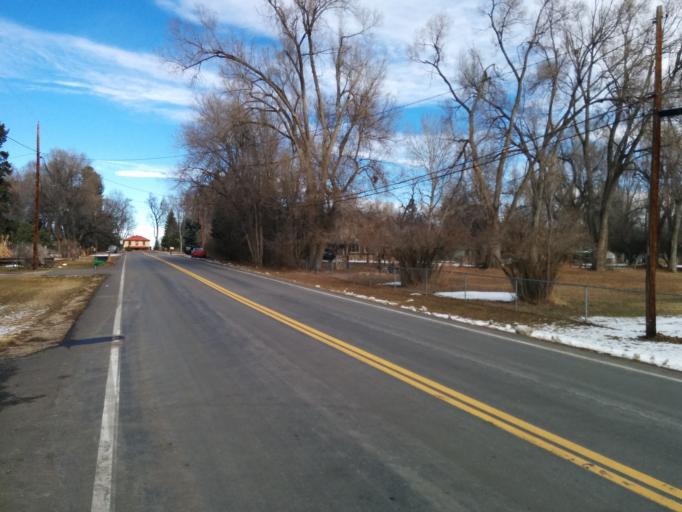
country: US
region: Colorado
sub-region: Larimer County
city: Laporte
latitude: 40.5946
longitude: -105.1259
